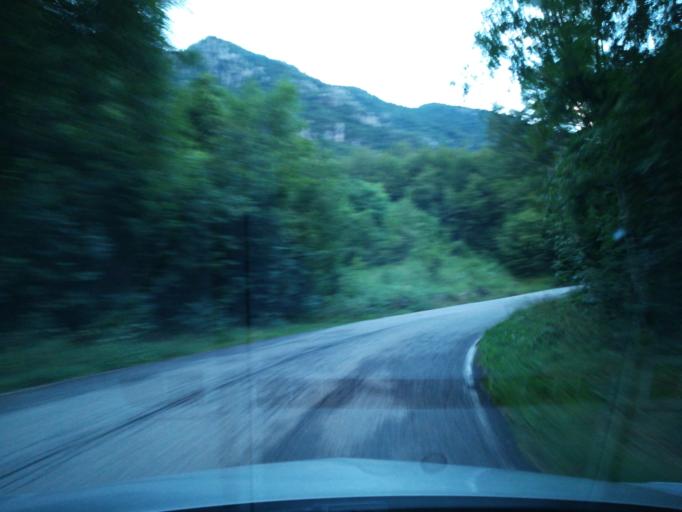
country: IT
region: Lombardy
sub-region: Provincia di Bergamo
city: Valsecca
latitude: 45.8209
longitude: 9.4847
